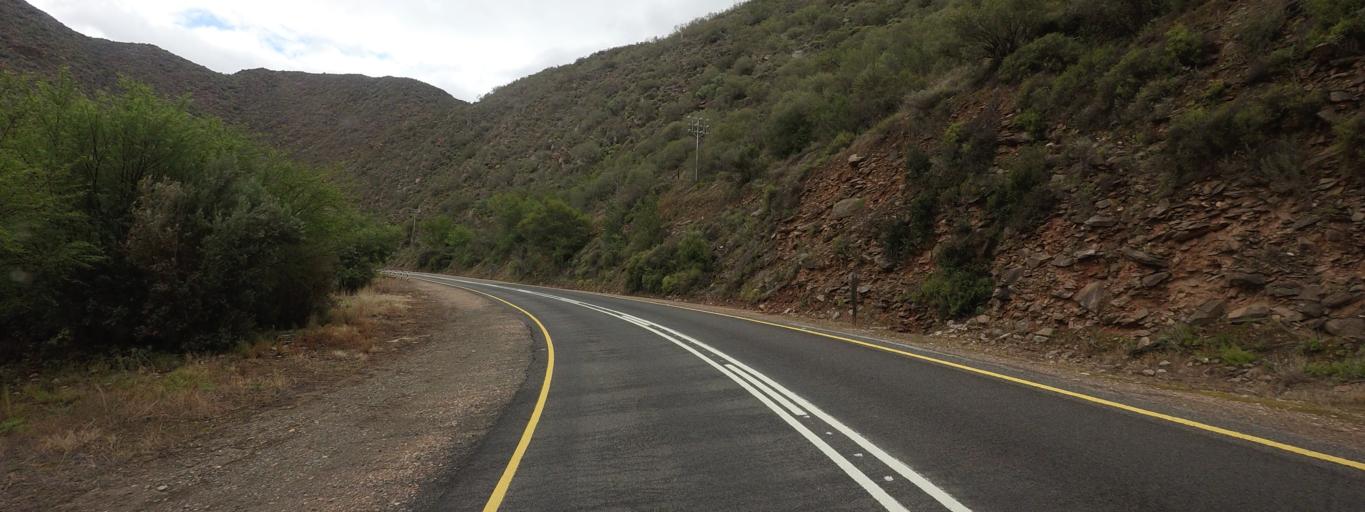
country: ZA
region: Western Cape
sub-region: Eden District Municipality
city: Oudtshoorn
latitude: -33.4252
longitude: 22.2503
